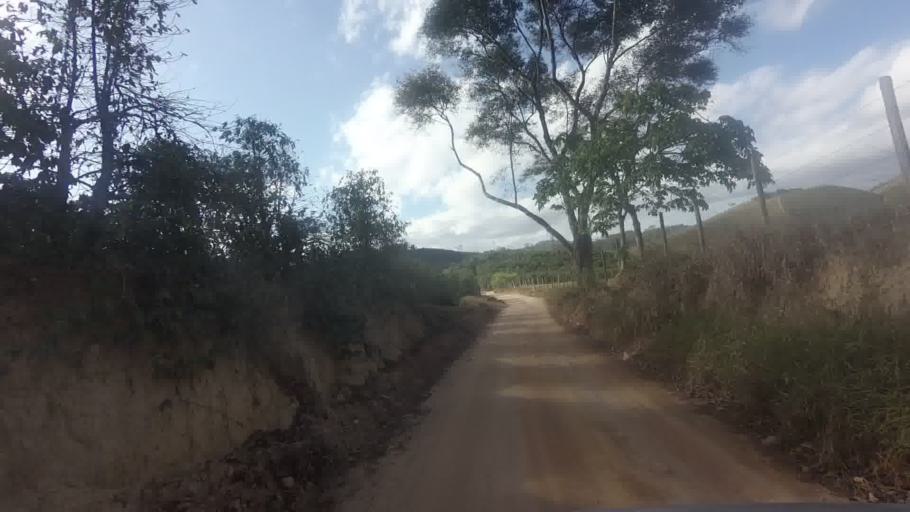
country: BR
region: Espirito Santo
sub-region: Sao Jose Do Calcado
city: Sao Jose do Calcado
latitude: -20.9837
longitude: -41.5137
